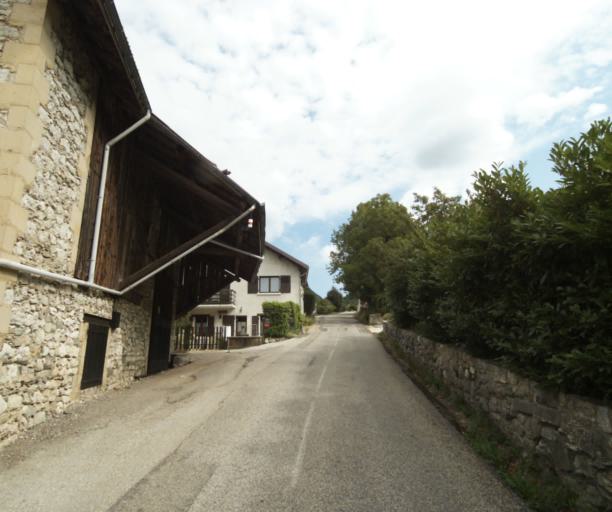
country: FR
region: Rhone-Alpes
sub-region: Departement de l'Isere
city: Saint-Egreve
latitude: 45.2817
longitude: 5.7104
